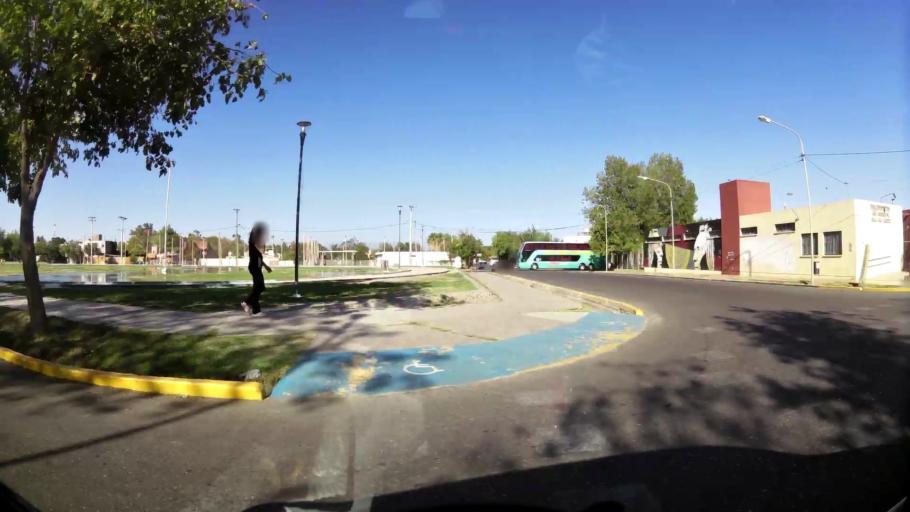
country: AR
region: San Juan
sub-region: Departamento de Santa Lucia
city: Santa Lucia
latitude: -31.5402
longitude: -68.5099
